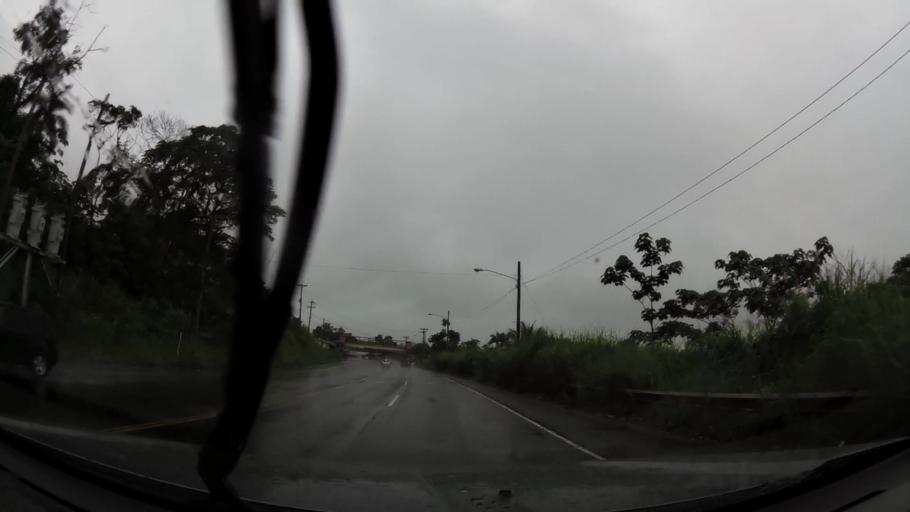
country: PA
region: Colon
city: Santa Rita Arriba
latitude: 9.3311
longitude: -79.8026
